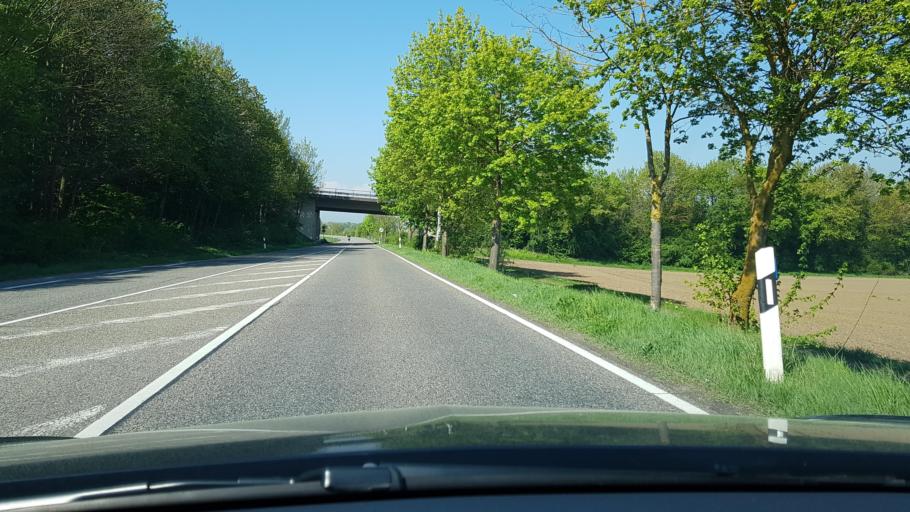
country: DE
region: Rheinland-Pfalz
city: Ochtendung
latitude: 50.3541
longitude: 7.4107
